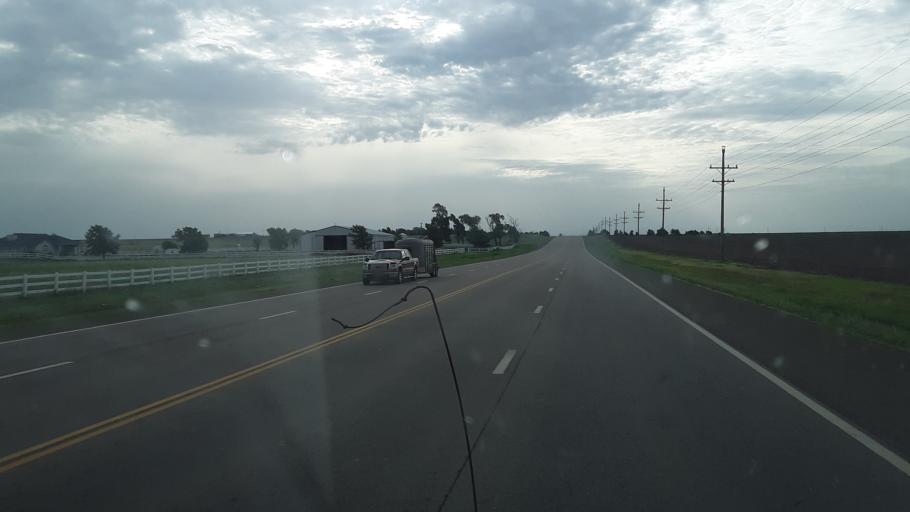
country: US
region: Kansas
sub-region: Finney County
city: Garden City
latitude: 37.9602
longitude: -100.8054
